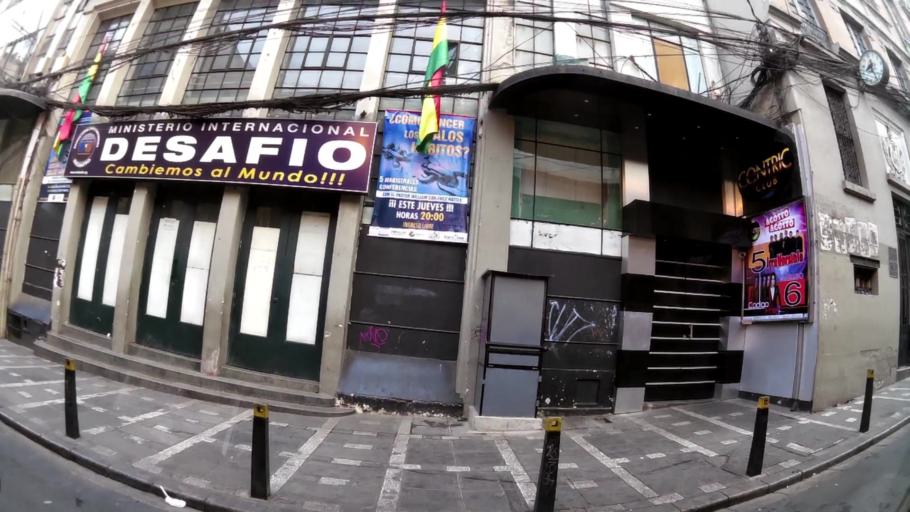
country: BO
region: La Paz
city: La Paz
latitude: -16.4987
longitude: -68.1341
